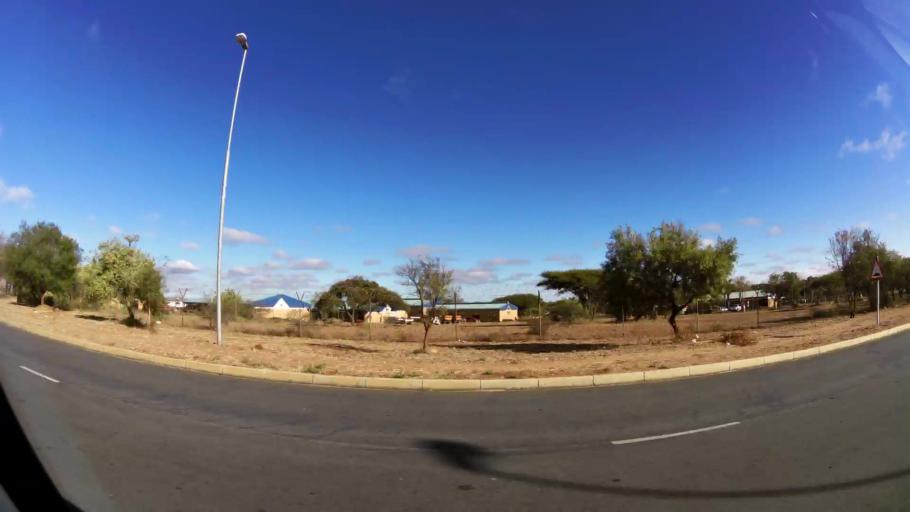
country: ZA
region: Limpopo
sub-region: Capricorn District Municipality
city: Polokwane
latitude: -23.9199
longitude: 29.4765
